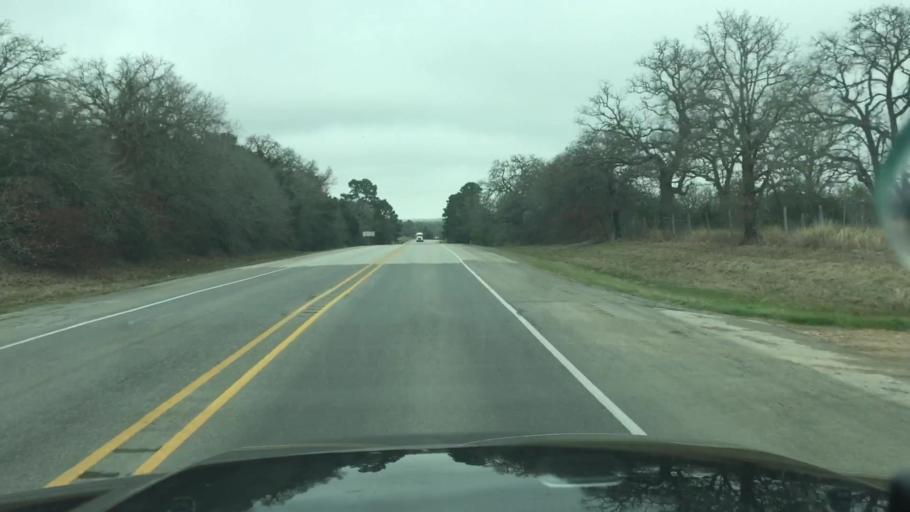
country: US
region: Texas
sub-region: Lee County
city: Giddings
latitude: 30.0770
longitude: -96.9171
